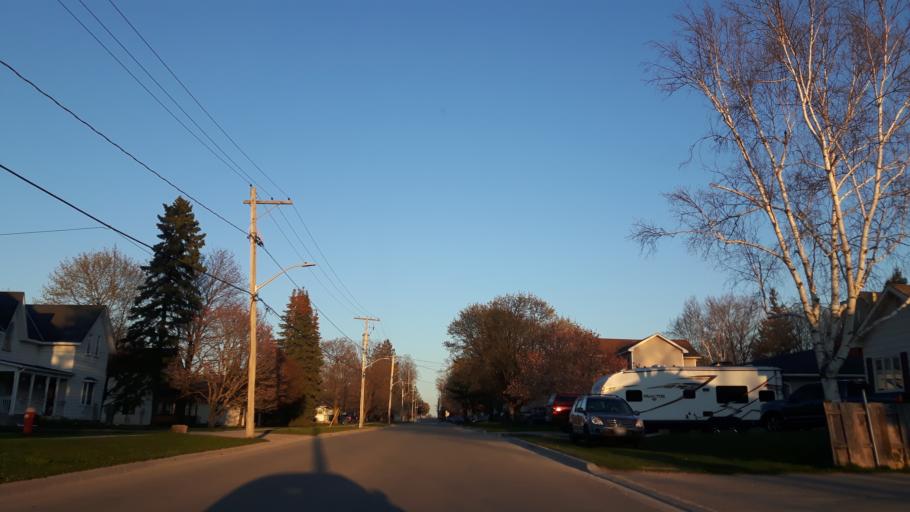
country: CA
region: Ontario
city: Bluewater
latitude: 43.6187
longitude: -81.5385
